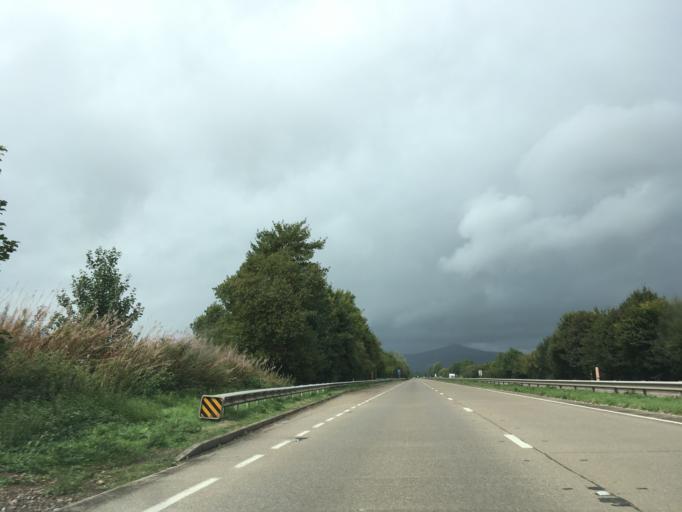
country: GB
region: Wales
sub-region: Monmouthshire
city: Abergavenny
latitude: 51.7940
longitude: -2.9944
